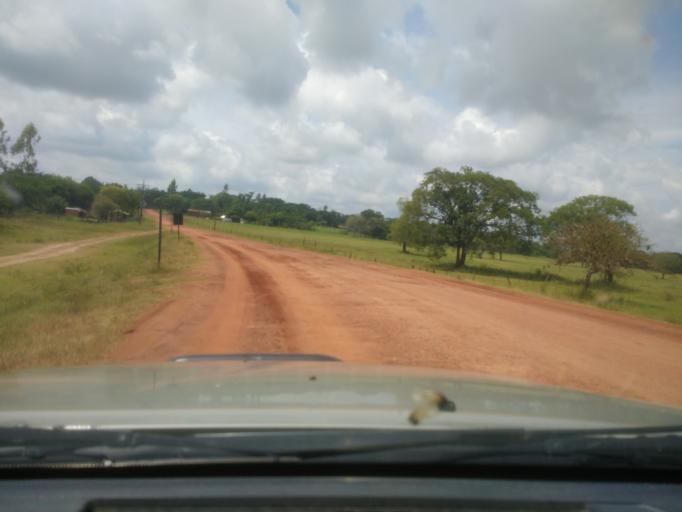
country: PY
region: San Pedro
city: Puerto Rosario
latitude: -24.4083
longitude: -57.1036
